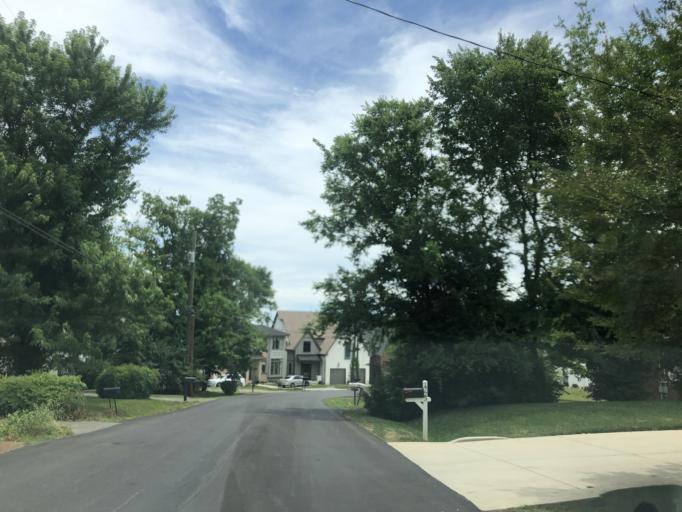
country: US
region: Tennessee
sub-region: Davidson County
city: Oak Hill
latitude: 36.1090
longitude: -86.8041
